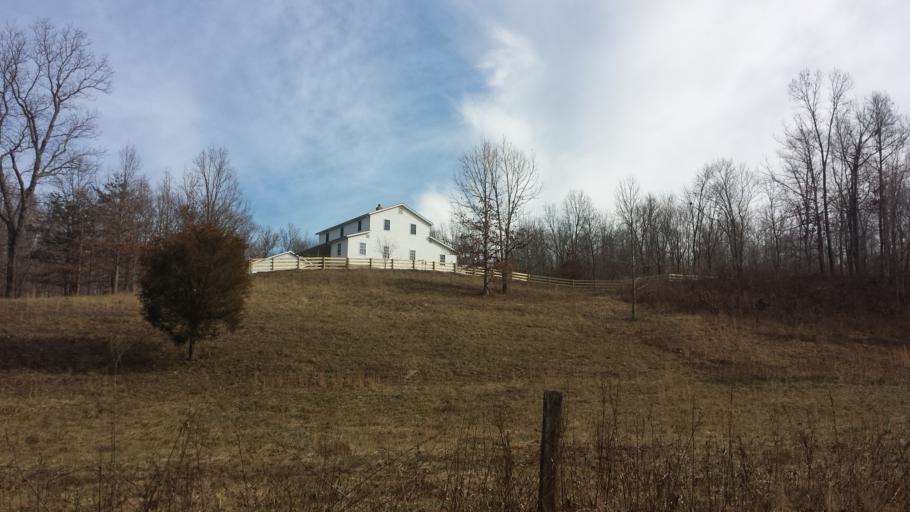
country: US
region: Ohio
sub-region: Gallia County
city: Gallipolis
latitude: 38.7200
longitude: -82.3498
